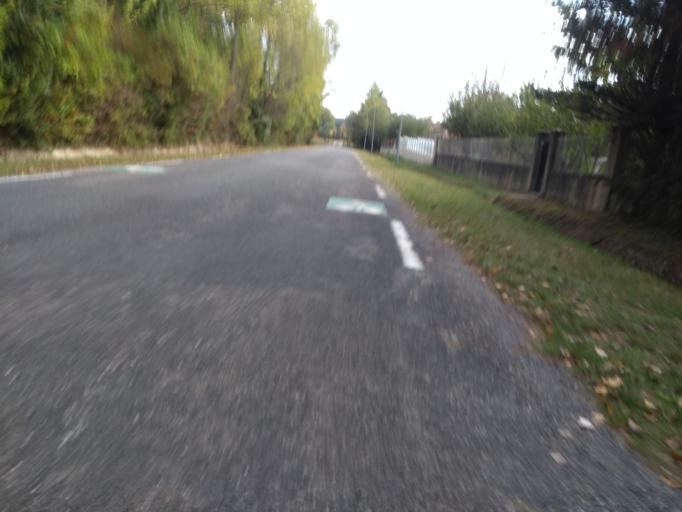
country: FR
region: Aquitaine
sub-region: Departement de la Gironde
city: Canejan
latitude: 44.7686
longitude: -0.6259
